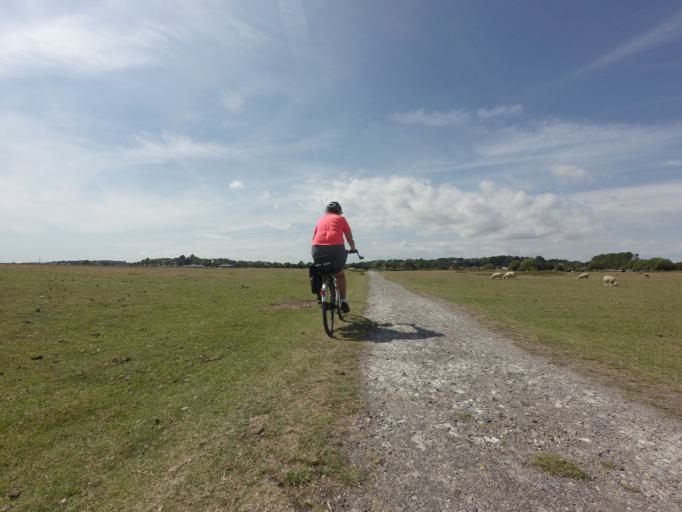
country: GB
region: England
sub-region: East Sussex
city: Rye
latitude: 50.9502
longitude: 0.7472
